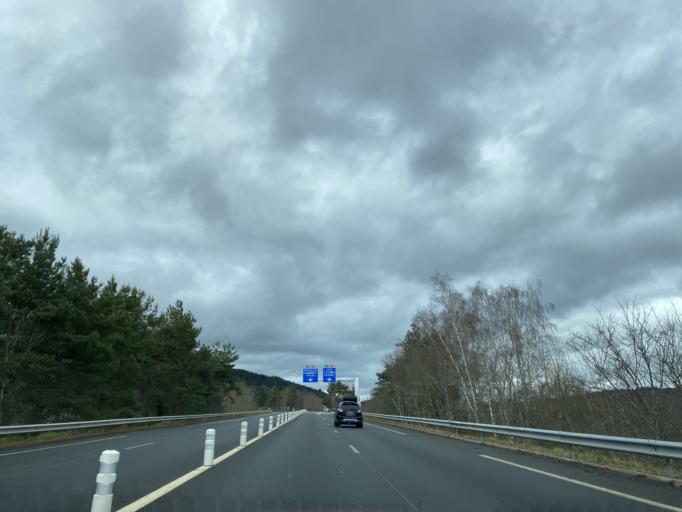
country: FR
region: Rhone-Alpes
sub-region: Departement de la Loire
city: Noiretable
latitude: 45.8510
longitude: 3.7928
